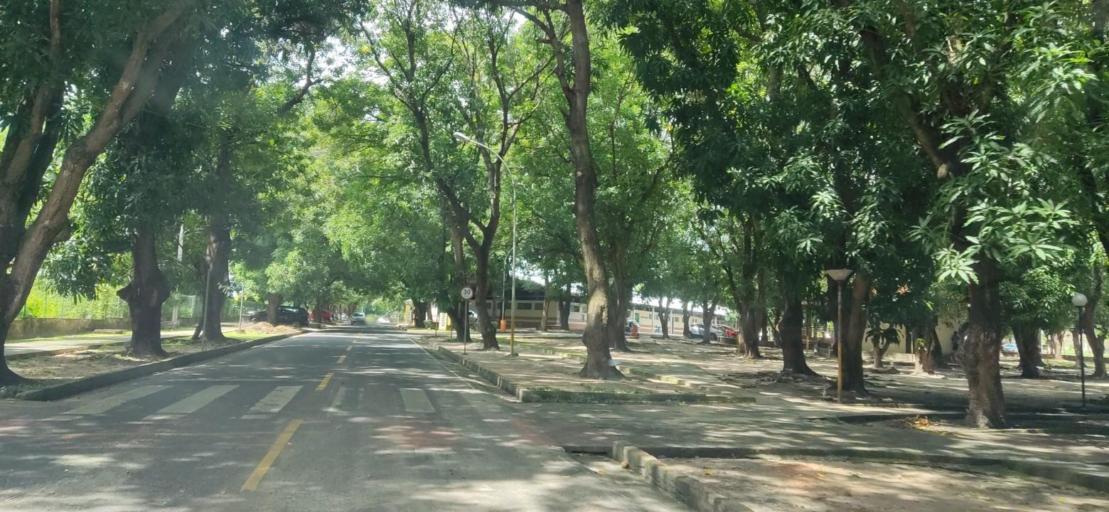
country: BR
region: Piaui
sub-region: Teresina
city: Teresina
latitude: -5.0580
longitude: -42.7928
